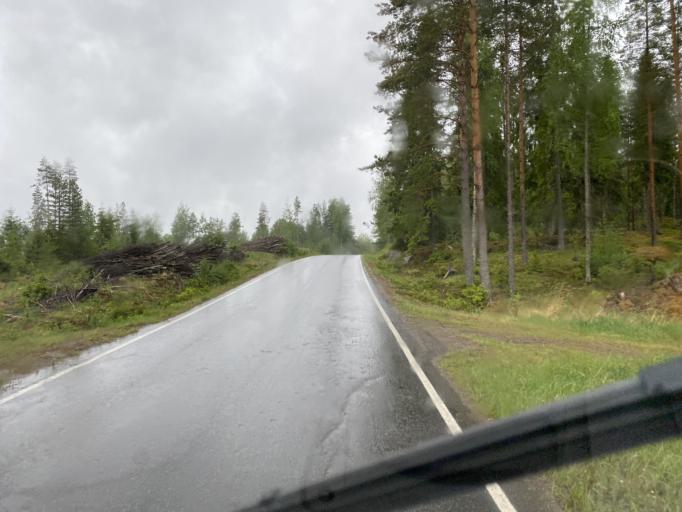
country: FI
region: Haeme
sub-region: Forssa
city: Humppila
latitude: 61.0818
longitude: 23.3115
